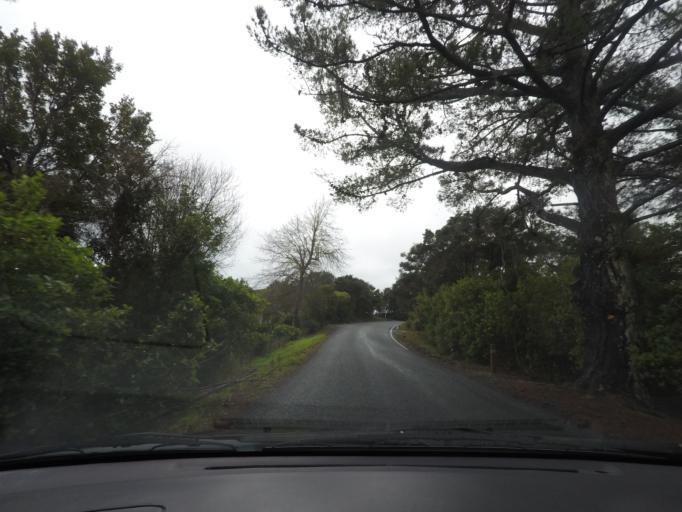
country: NZ
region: Auckland
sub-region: Auckland
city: Warkworth
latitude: -36.4761
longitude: 174.7325
